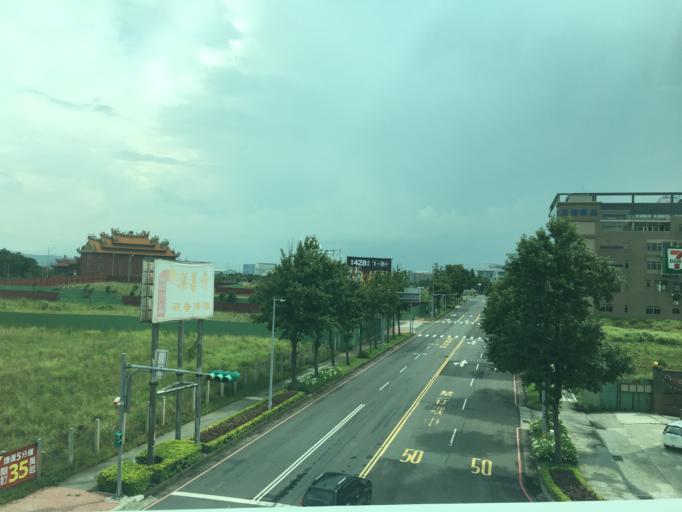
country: TW
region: Taiwan
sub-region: Taoyuan
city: Taoyuan
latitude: 25.0501
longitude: 121.3818
